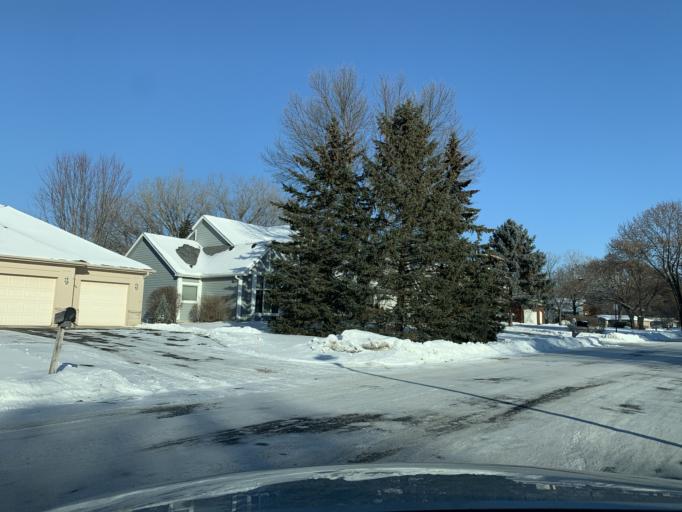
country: US
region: Minnesota
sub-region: Scott County
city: Savage
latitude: 44.8295
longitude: -93.3566
